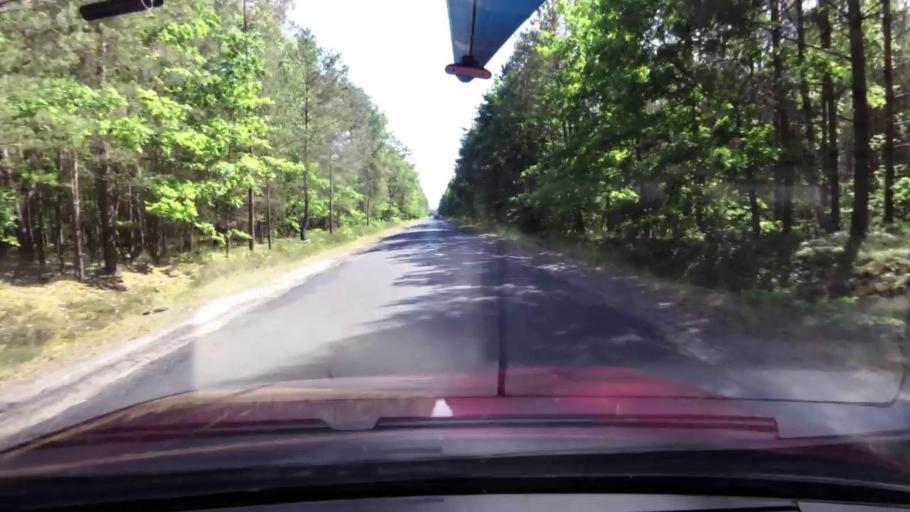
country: PL
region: Pomeranian Voivodeship
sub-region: Powiat slupski
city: Kepice
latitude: 54.3041
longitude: 16.9618
